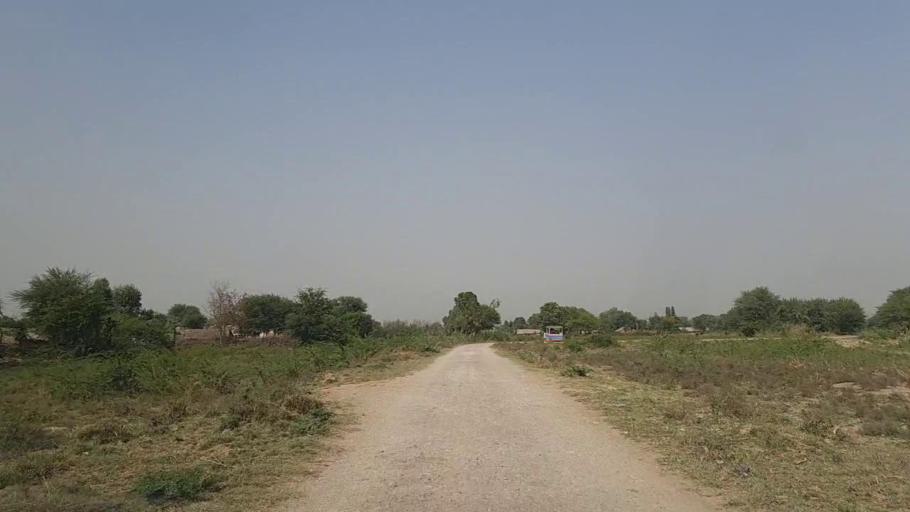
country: PK
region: Sindh
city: Samaro
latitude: 25.2823
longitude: 69.3734
